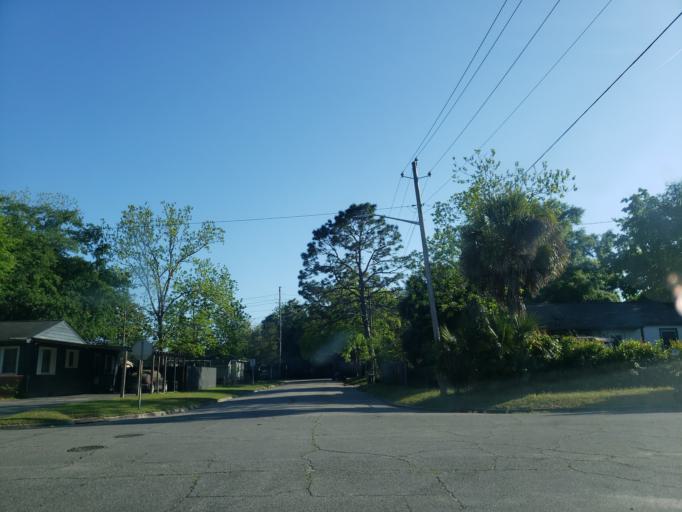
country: US
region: Georgia
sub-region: Chatham County
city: Thunderbolt
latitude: 32.0663
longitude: -81.0514
